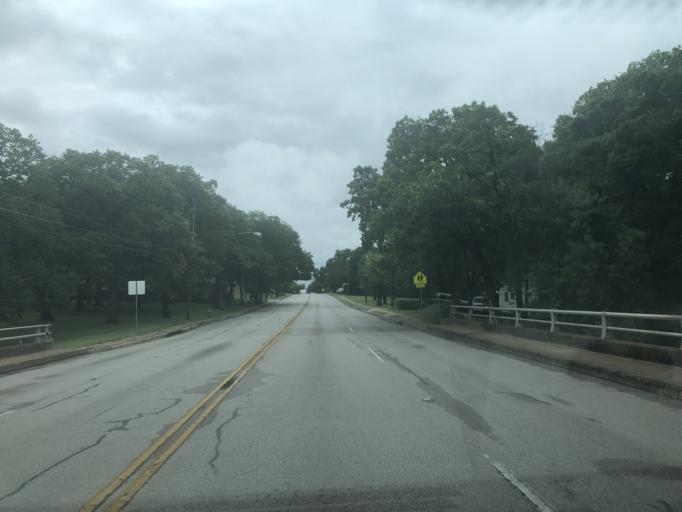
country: US
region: Texas
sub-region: Dallas County
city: Irving
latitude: 32.8011
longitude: -96.9451
